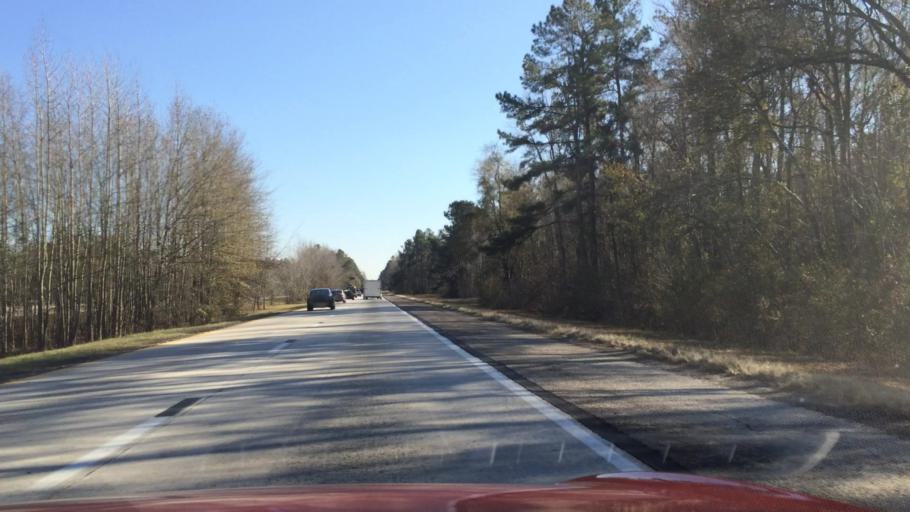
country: US
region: South Carolina
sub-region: Orangeburg County
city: Holly Hill
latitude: 33.2608
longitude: -80.4775
